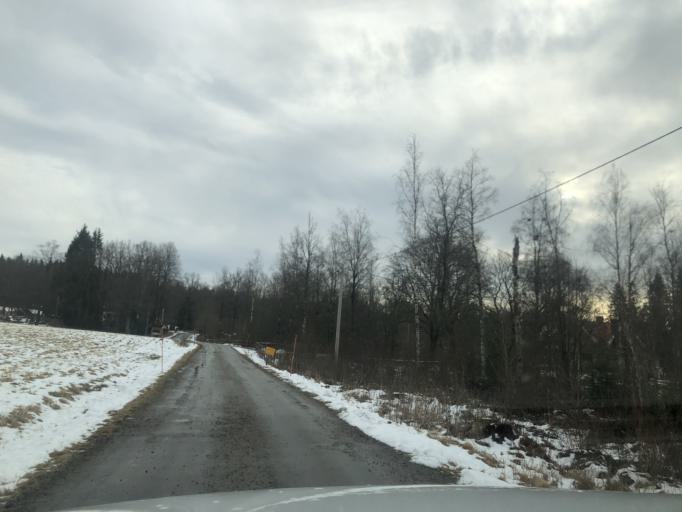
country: SE
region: Vaestra Goetaland
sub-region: Ulricehamns Kommun
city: Ulricehamn
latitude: 57.7711
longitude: 13.4693
